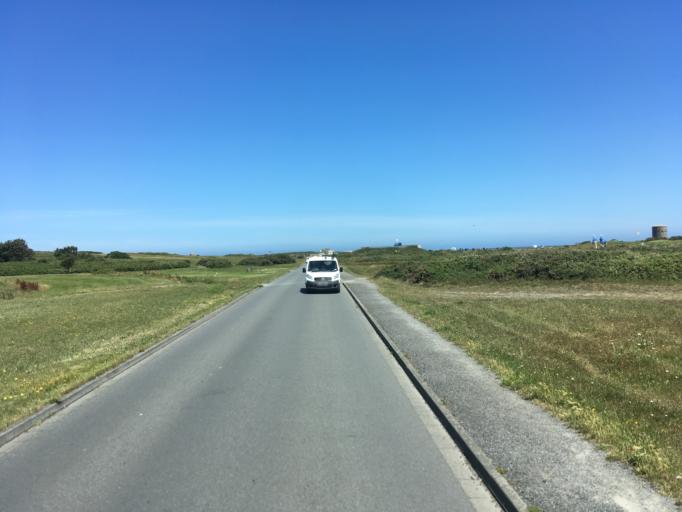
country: GG
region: St Peter Port
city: Saint Peter Port
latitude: 49.4998
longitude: -2.5334
